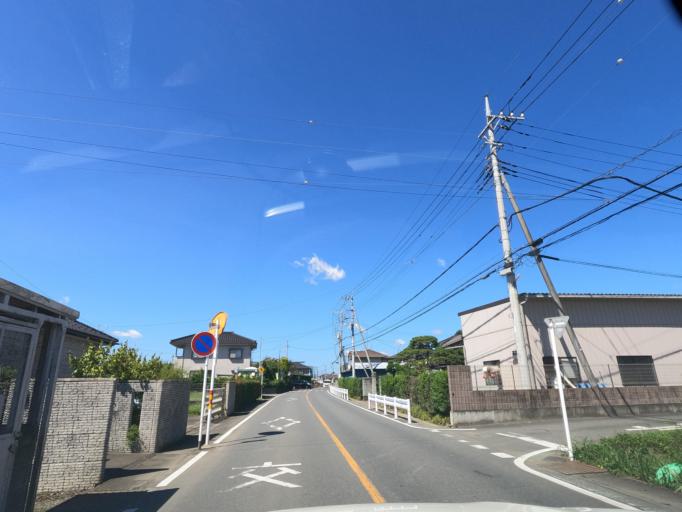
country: JP
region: Saitama
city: Kamifukuoka
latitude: 35.9105
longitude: 139.5378
